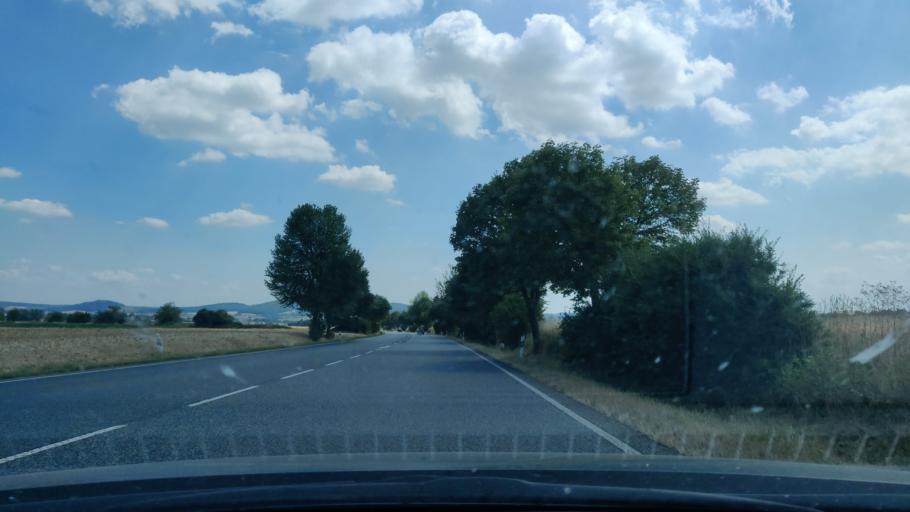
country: DE
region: Hesse
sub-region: Regierungsbezirk Kassel
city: Wabern
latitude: 51.0964
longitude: 9.3067
